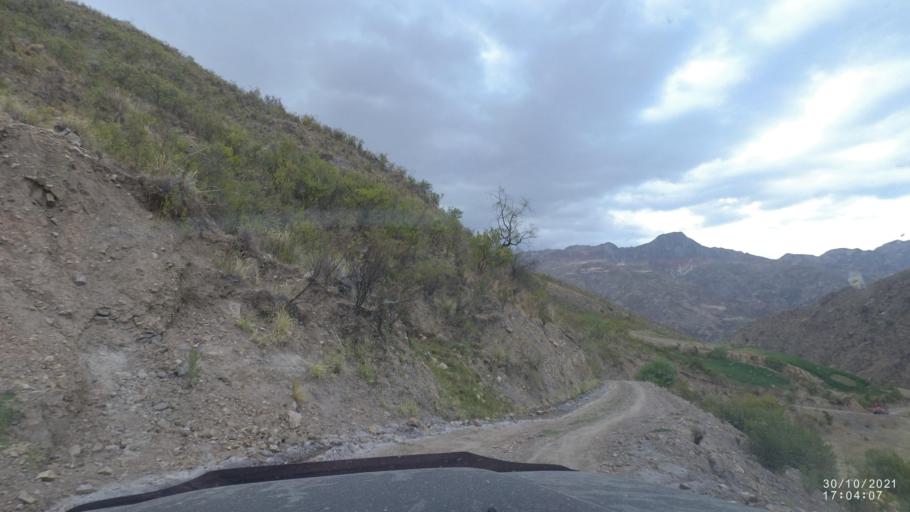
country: BO
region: Cochabamba
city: Colchani
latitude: -17.5679
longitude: -66.6311
